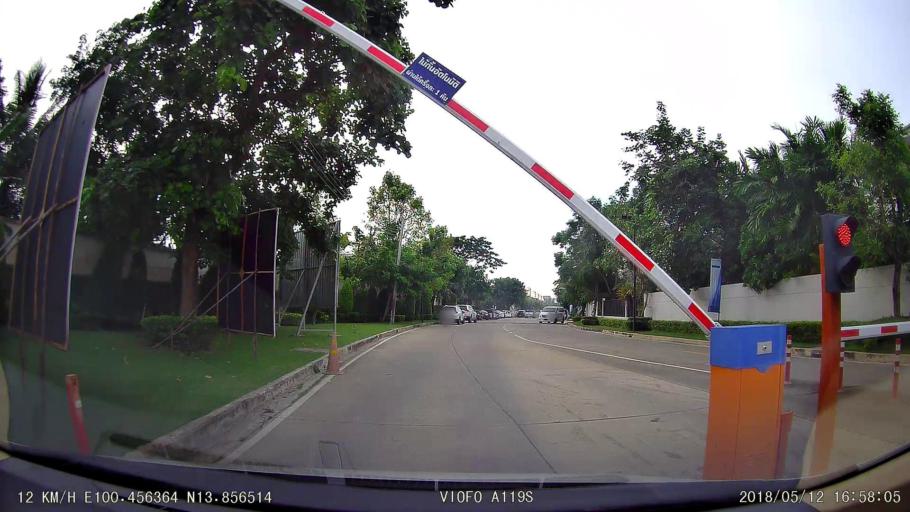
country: TH
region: Nonthaburi
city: Bang Kruai
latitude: 13.8563
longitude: 100.4566
